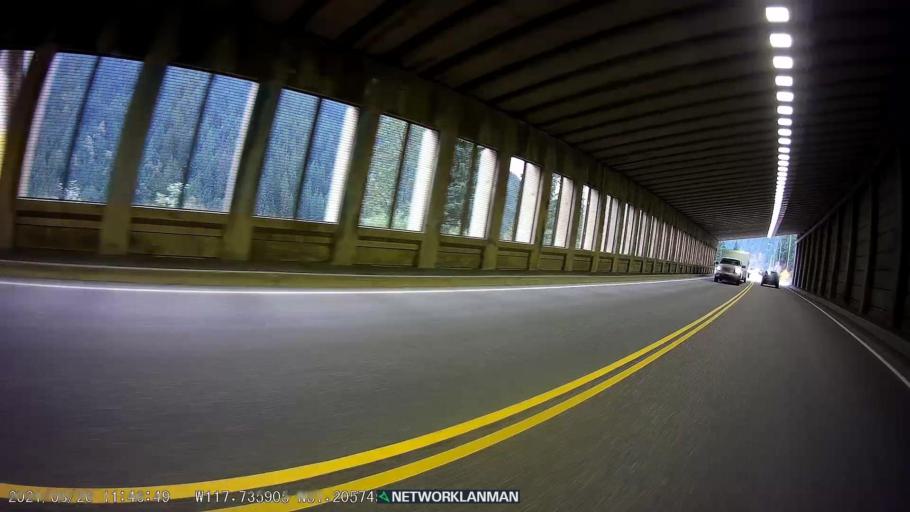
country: CA
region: British Columbia
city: Revelstoke
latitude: 51.2056
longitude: -117.7362
